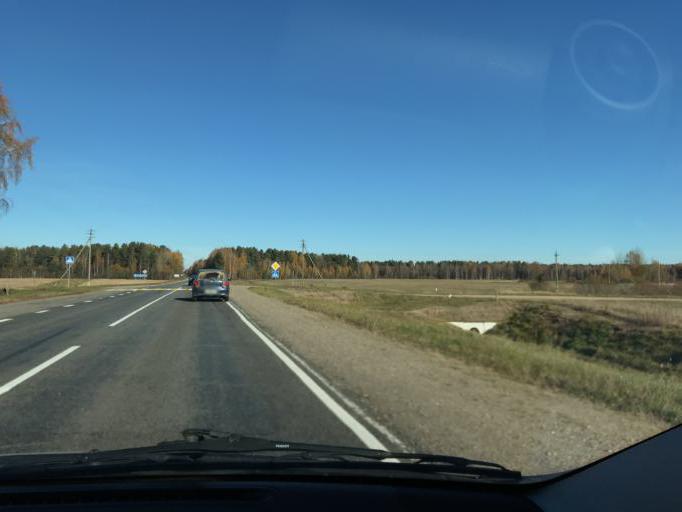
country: BY
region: Vitebsk
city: Lyepyel'
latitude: 55.0563
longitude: 28.7519
